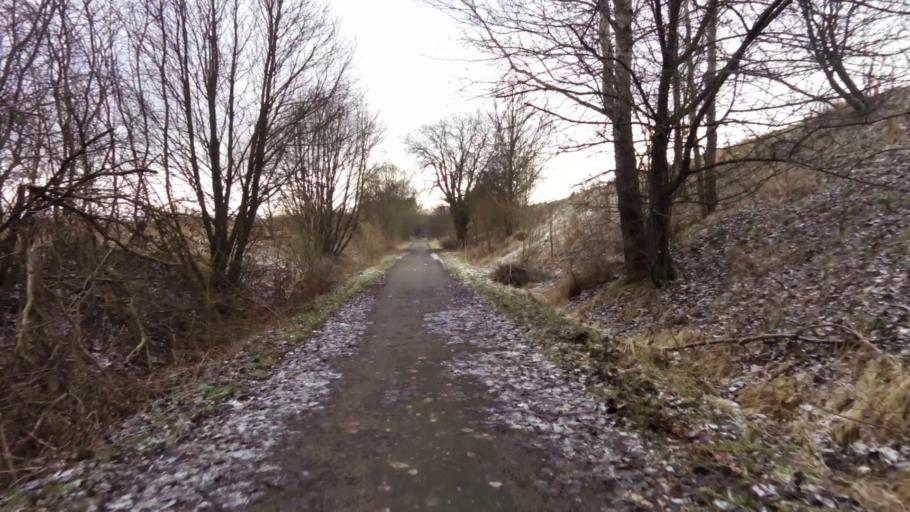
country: PL
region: West Pomeranian Voivodeship
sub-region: Powiat drawski
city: Zlocieniec
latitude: 53.5997
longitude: 16.0463
